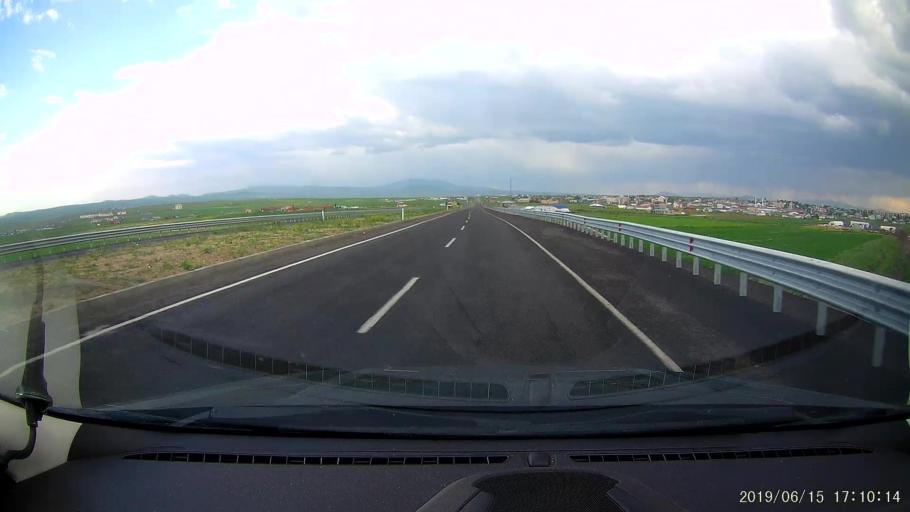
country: TR
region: Kars
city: Kars
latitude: 40.6244
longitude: 43.1339
